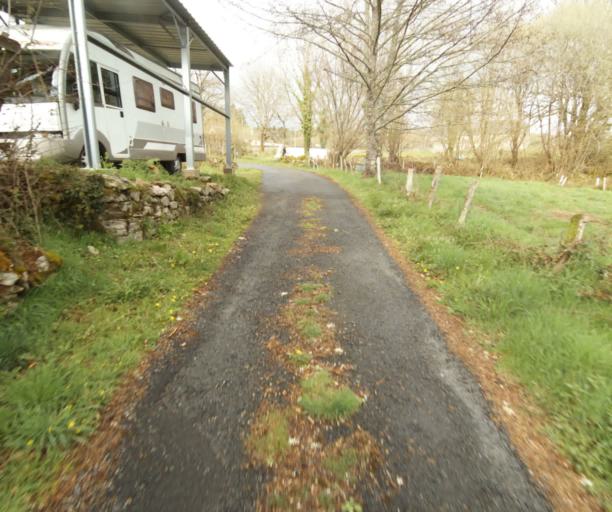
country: FR
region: Limousin
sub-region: Departement de la Correze
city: Saint-Privat
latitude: 45.2269
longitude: 1.9999
